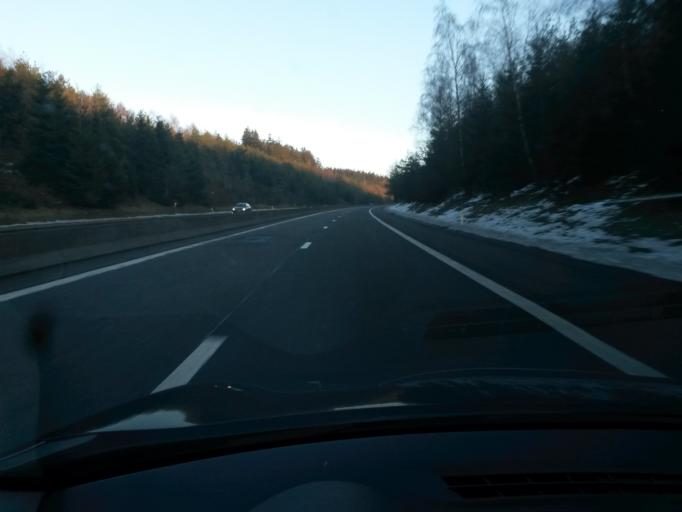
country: BE
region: Wallonia
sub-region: Province de Liege
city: Waimes
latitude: 50.3557
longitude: 6.0629
